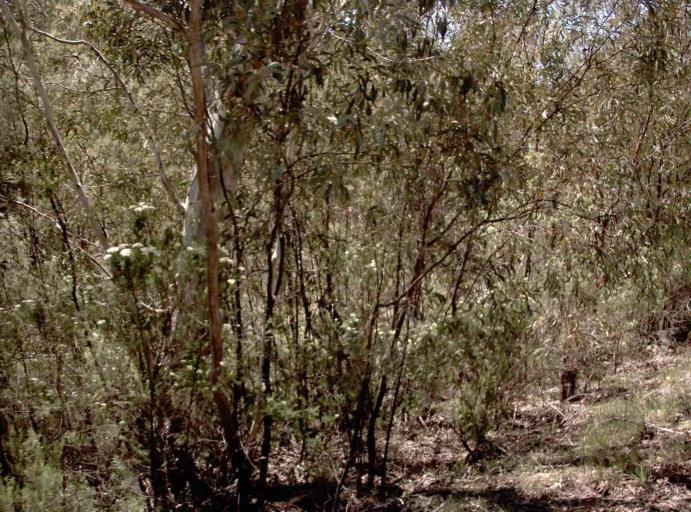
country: AU
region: New South Wales
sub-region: Snowy River
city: Jindabyne
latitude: -37.0650
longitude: 148.2973
